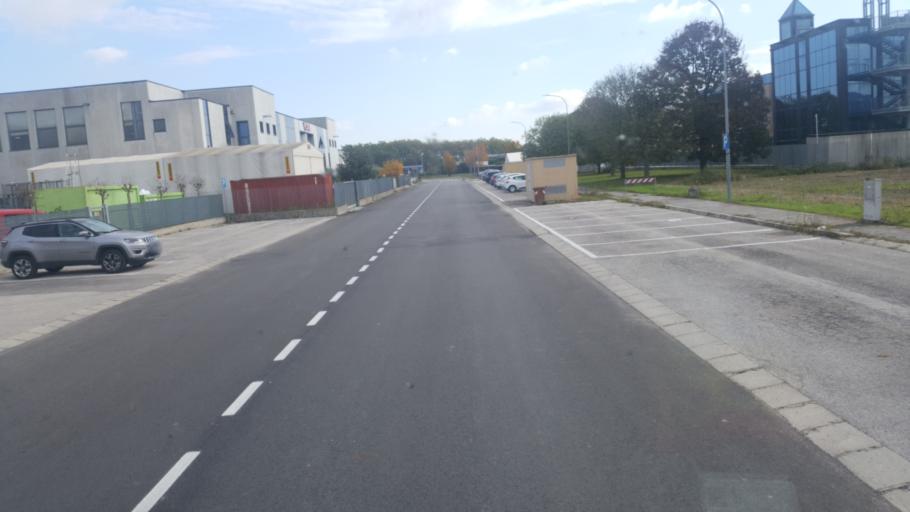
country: IT
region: Veneto
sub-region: Provincia di Vicenza
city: Ponte di Castegnero
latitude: 45.4425
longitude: 11.5975
